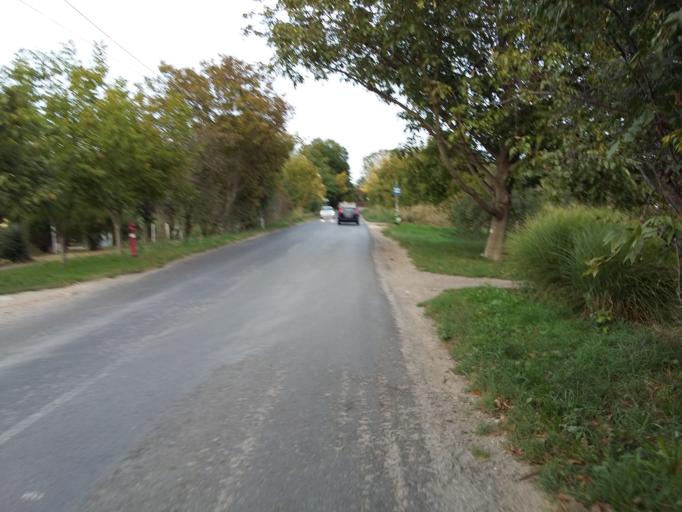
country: HU
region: Csongrad
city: Szeged
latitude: 46.2255
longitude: 20.1106
